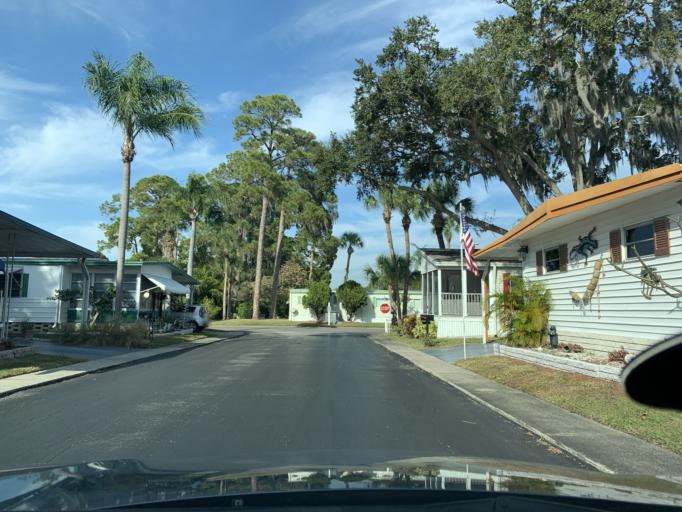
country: US
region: Florida
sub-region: Pinellas County
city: Largo
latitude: 27.8991
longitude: -82.7776
